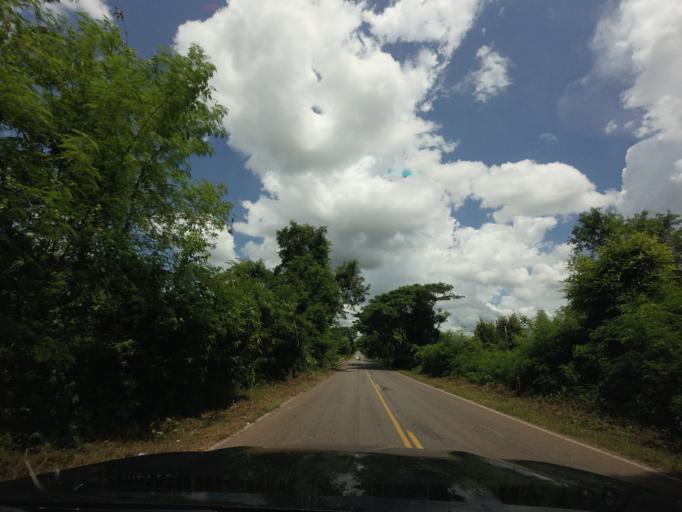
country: TH
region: Changwat Udon Thani
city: Phibun Rak
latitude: 17.5927
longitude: 103.0543
